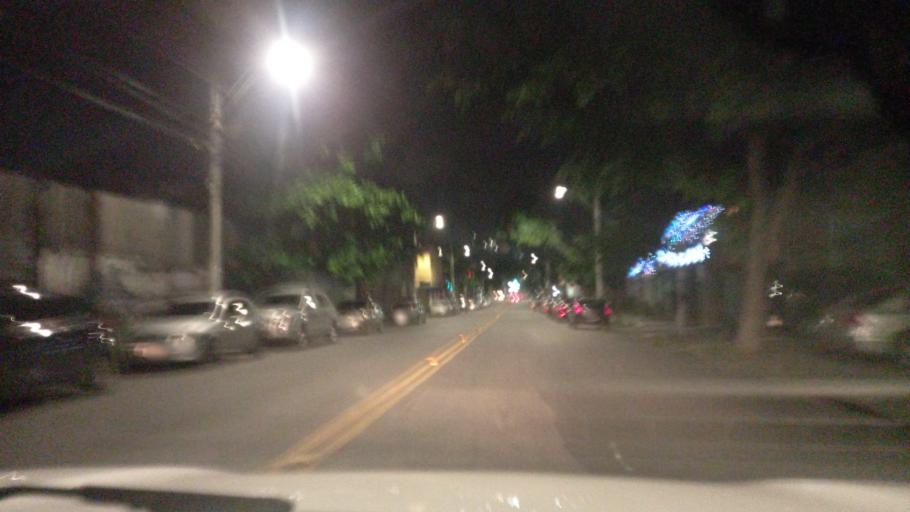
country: BR
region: Minas Gerais
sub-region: Belo Horizonte
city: Belo Horizonte
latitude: -19.8854
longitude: -43.9399
